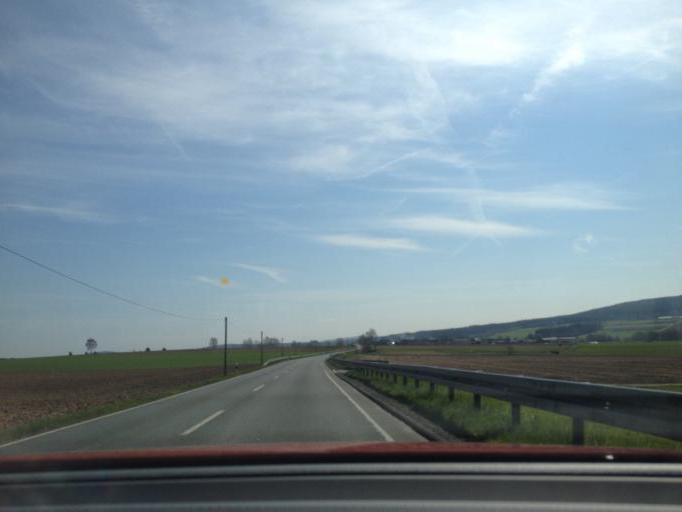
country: DE
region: Bavaria
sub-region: Upper Franconia
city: Oberhaid
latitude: 50.0963
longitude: 11.8317
